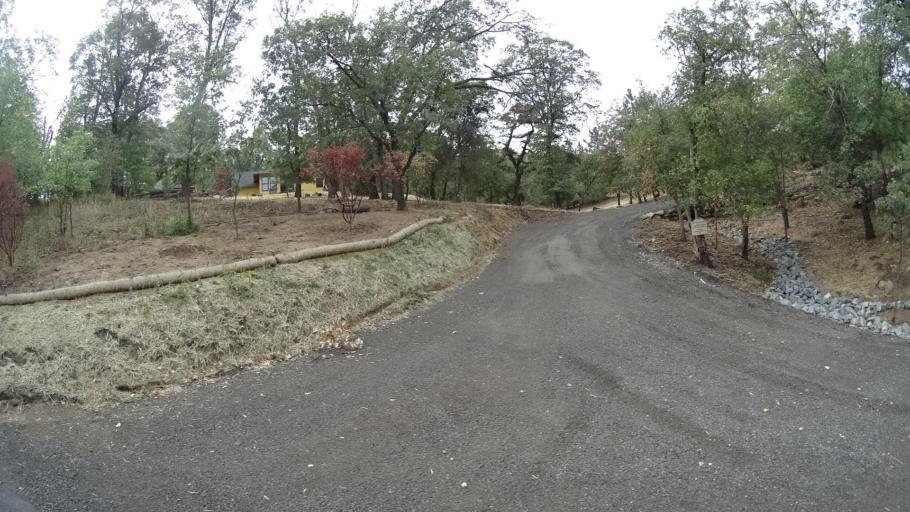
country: US
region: California
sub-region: San Diego County
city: Julian
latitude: 33.0531
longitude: -116.6251
